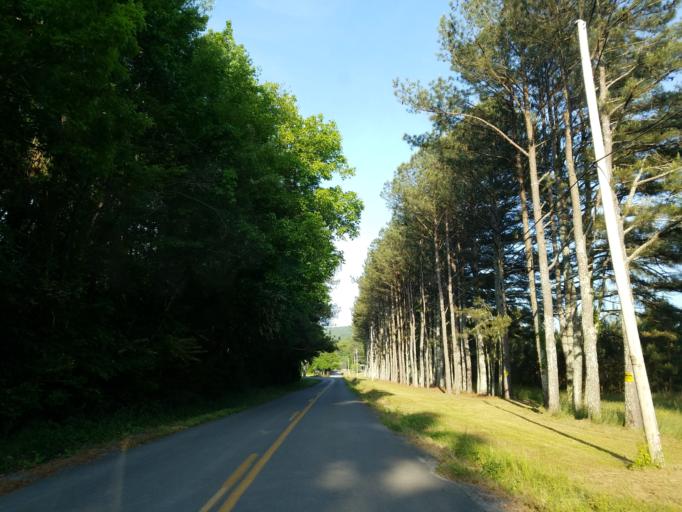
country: US
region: Georgia
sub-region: Gordon County
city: Calhoun
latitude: 34.5289
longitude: -85.1140
